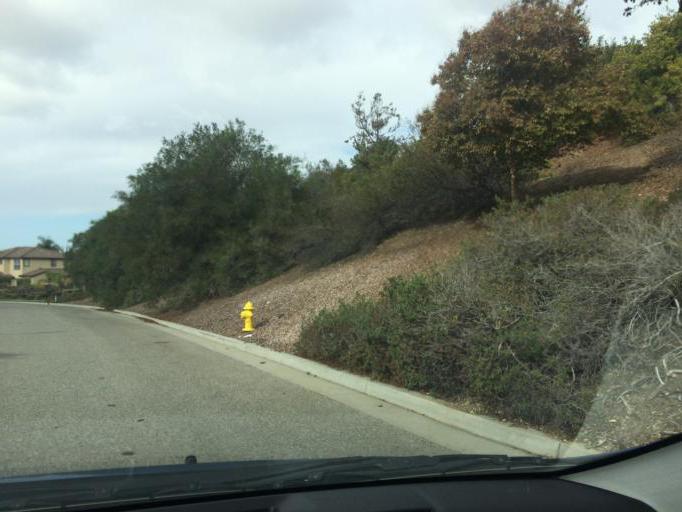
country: US
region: California
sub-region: Santa Clara County
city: Seven Trees
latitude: 37.2827
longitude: -121.7915
